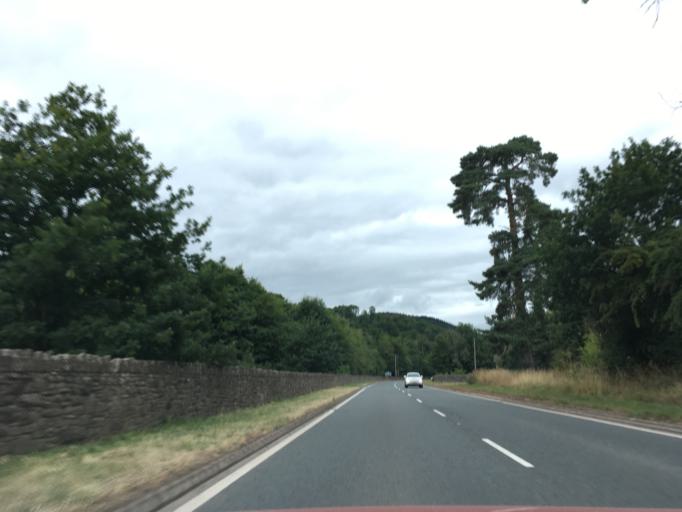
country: GB
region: Wales
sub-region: Blaenau Gwent
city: Brynmawr
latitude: 51.8727
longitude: -3.1726
